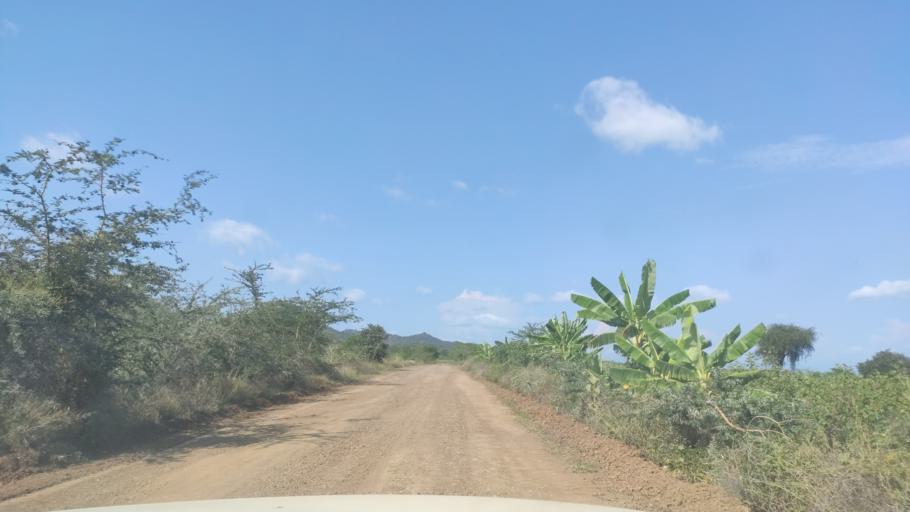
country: ET
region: Southern Nations, Nationalities, and People's Region
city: Felege Neway
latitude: 6.3921
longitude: 37.0995
